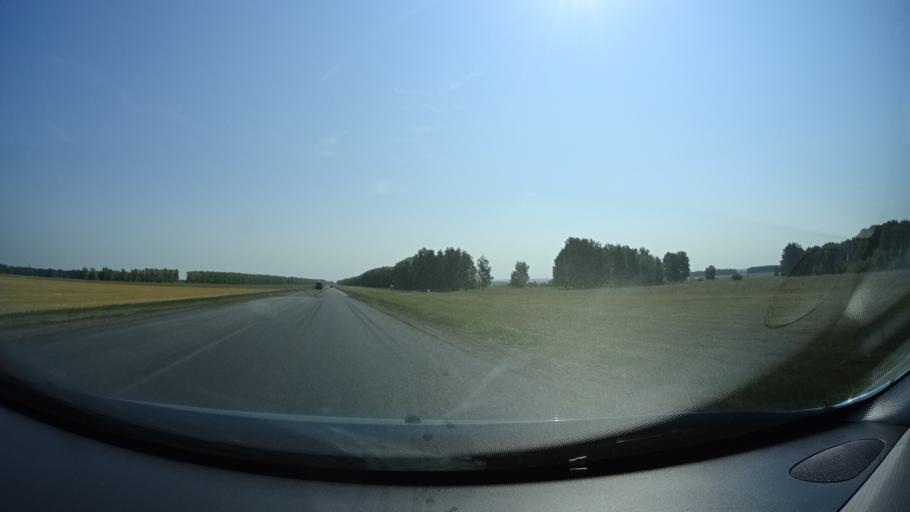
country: RU
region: Bashkortostan
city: Karmaskaly
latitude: 54.3999
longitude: 56.0951
